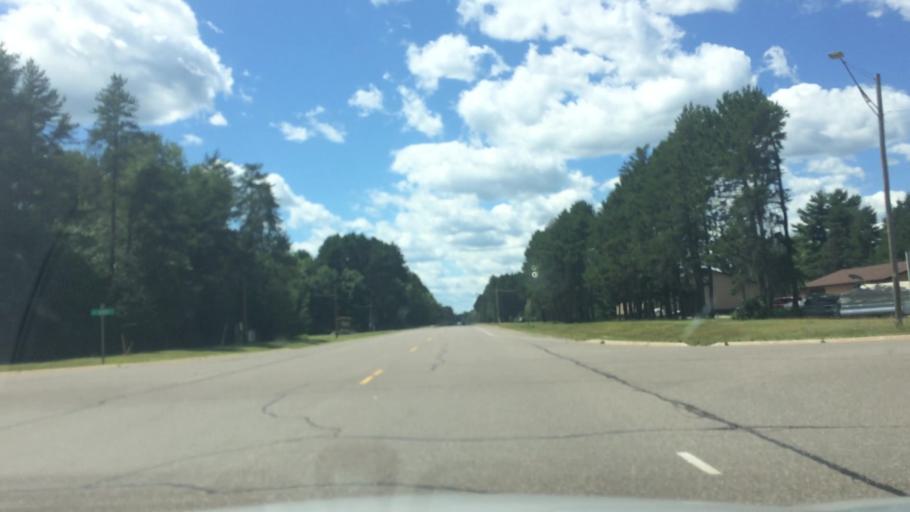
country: US
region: Wisconsin
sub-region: Vilas County
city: Lac du Flambeau
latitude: 45.8833
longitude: -89.7457
